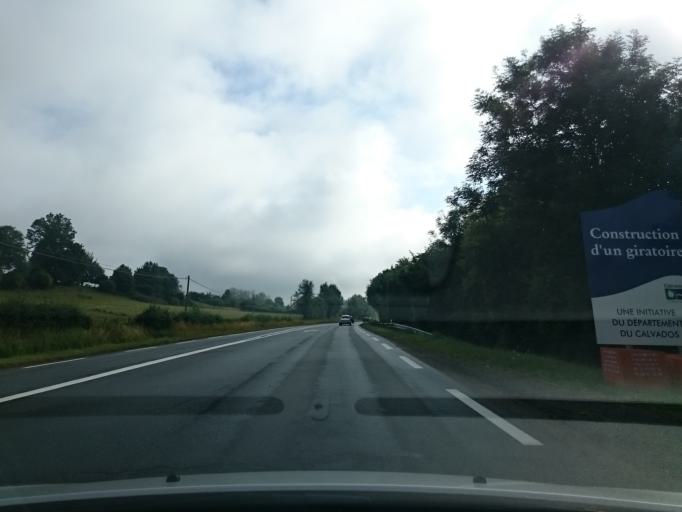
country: FR
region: Lower Normandy
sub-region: Departement du Calvados
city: Cambremer
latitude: 49.1300
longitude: 0.1110
